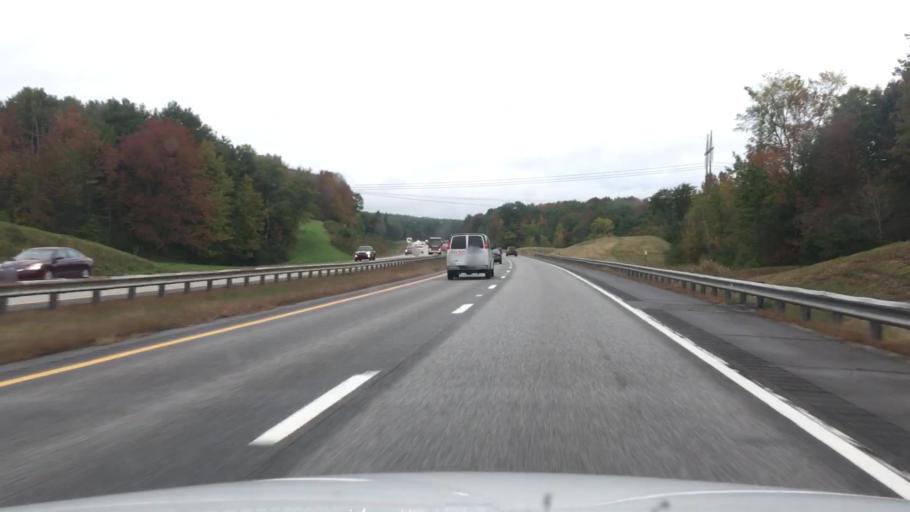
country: US
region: Maine
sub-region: Cumberland County
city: Cumberland Center
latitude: 43.7558
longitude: -70.3051
